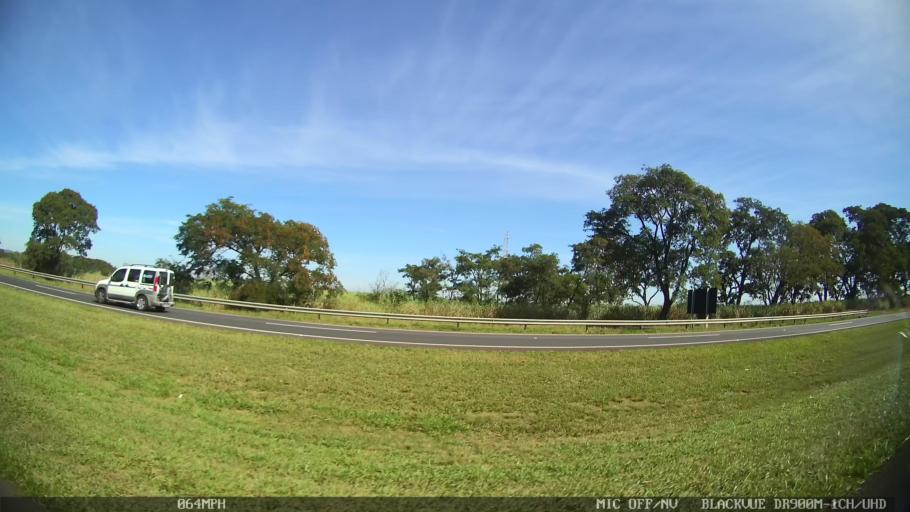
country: BR
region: Sao Paulo
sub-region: Porto Ferreira
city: Porto Ferreira
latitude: -21.9045
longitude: -47.4777
